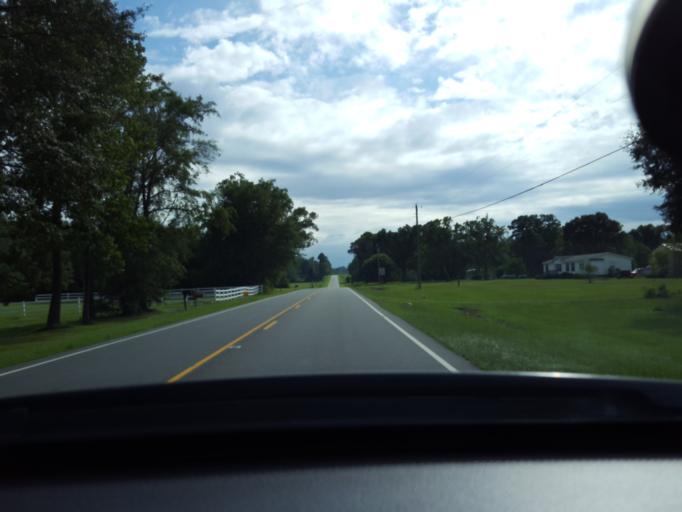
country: US
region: North Carolina
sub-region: Duplin County
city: Kenansville
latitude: 35.0030
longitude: -77.9136
